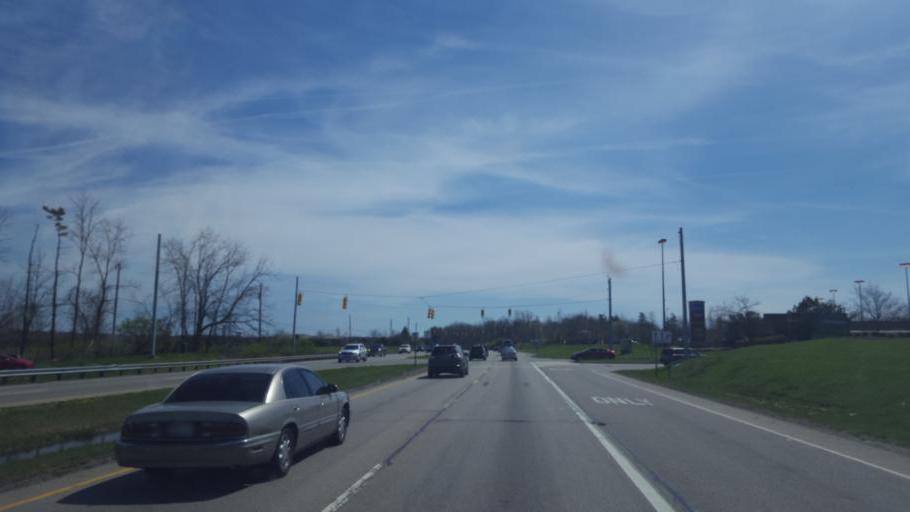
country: US
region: Ohio
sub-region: Delaware County
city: Delaware
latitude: 40.2671
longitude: -83.0703
